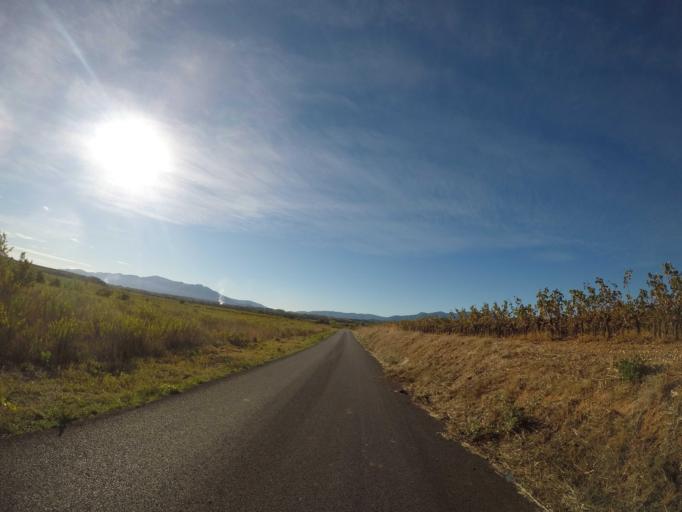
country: FR
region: Languedoc-Roussillon
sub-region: Departement des Pyrenees-Orientales
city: Llupia
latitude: 42.5935
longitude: 2.7642
